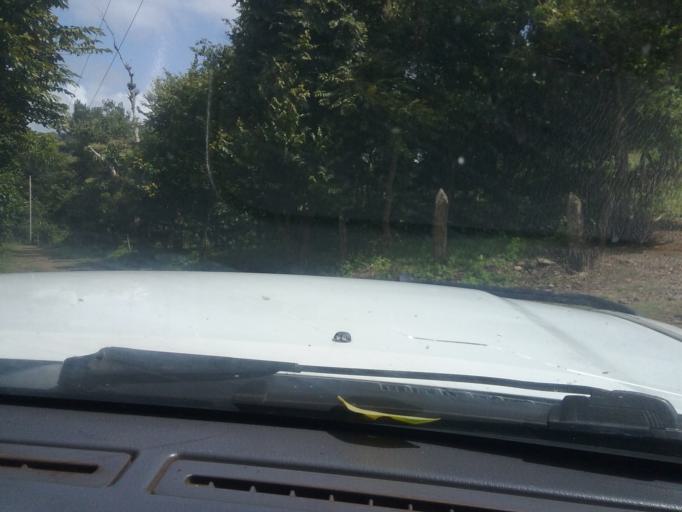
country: NI
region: Matagalpa
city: Matagalpa
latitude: 12.8652
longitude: -85.9098
